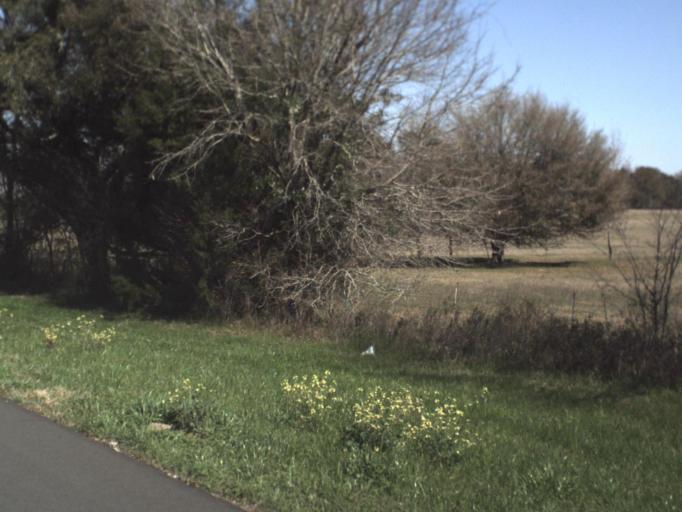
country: US
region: Florida
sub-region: Jackson County
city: Sneads
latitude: 30.7722
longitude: -85.0191
